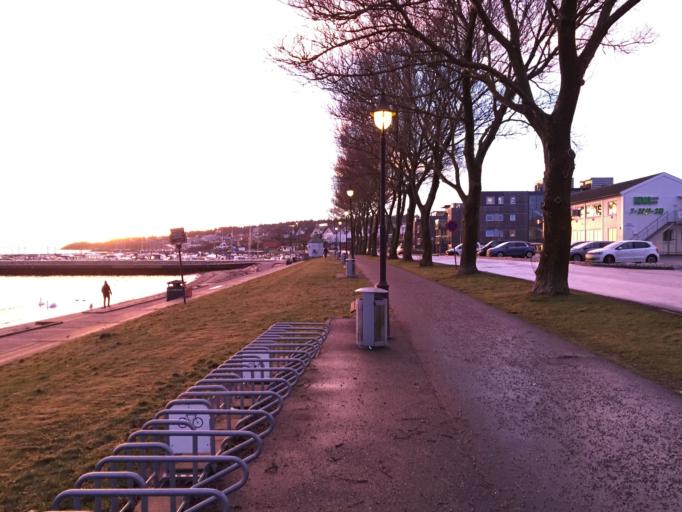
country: NO
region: Ostfold
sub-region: Moss
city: Moss
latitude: 59.4314
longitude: 10.6506
